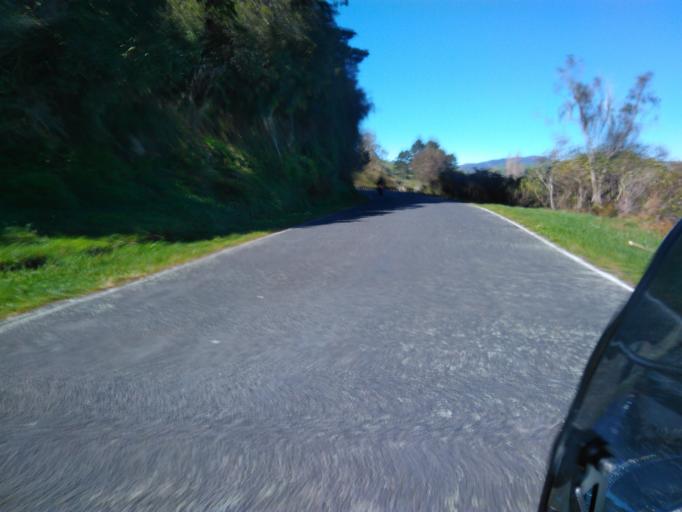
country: NZ
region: Bay of Plenty
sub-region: Opotiki District
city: Opotiki
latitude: -38.3312
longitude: 177.5326
